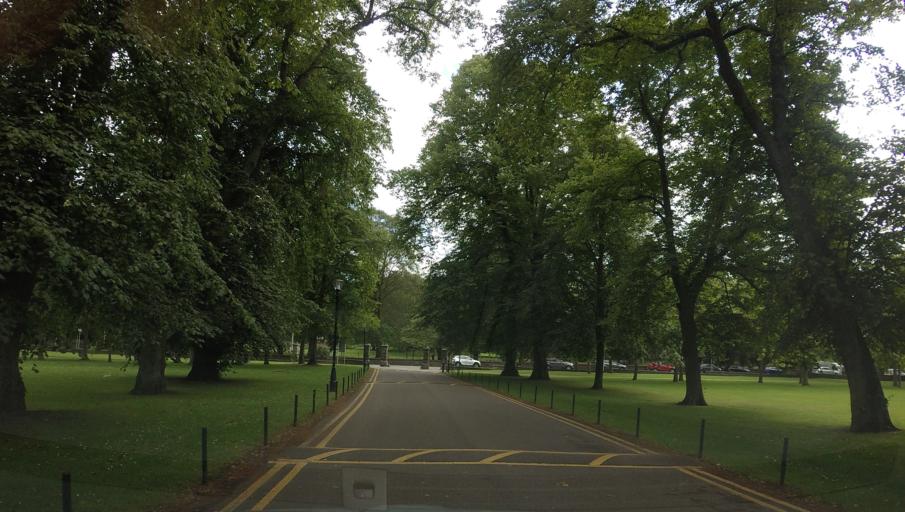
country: GB
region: Scotland
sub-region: Aberdeen City
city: Aberdeen
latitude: 57.1533
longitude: -2.1233
